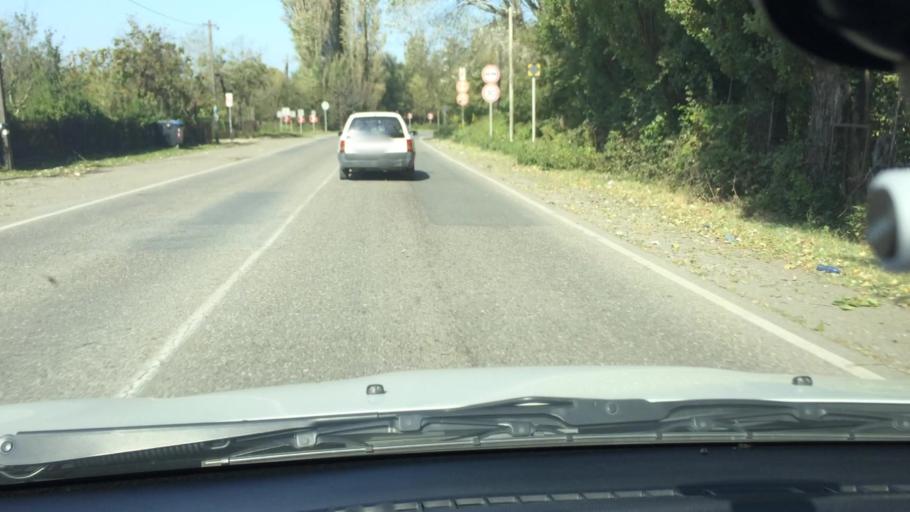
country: GE
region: Guria
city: Lanchkhuti
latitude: 42.0839
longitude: 41.9511
